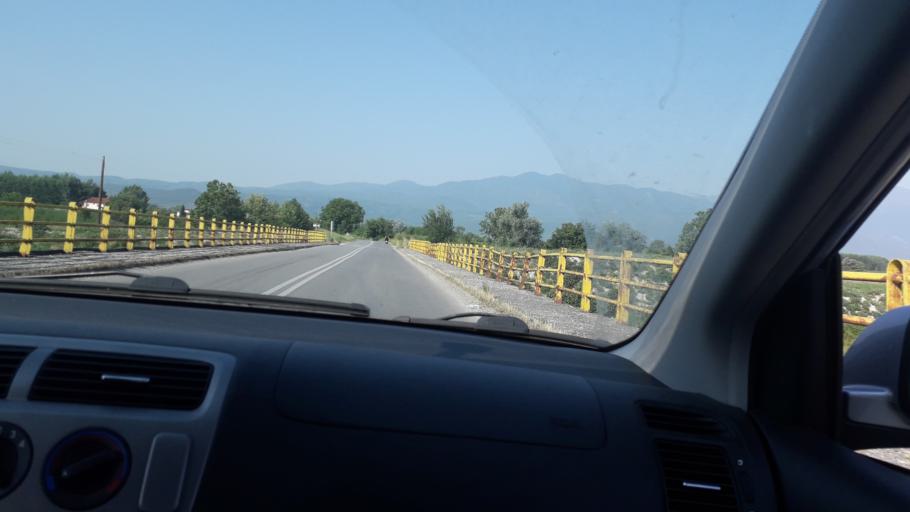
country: GR
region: Central Macedonia
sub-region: Nomos Pellis
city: Tsakoi
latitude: 40.9610
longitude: 22.0494
